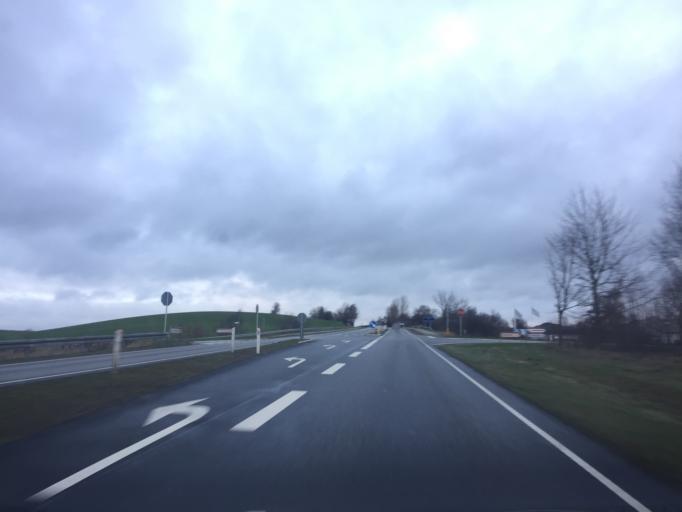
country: DK
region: Capital Region
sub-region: Frederikssund Kommune
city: Skibby
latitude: 55.7604
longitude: 11.9560
